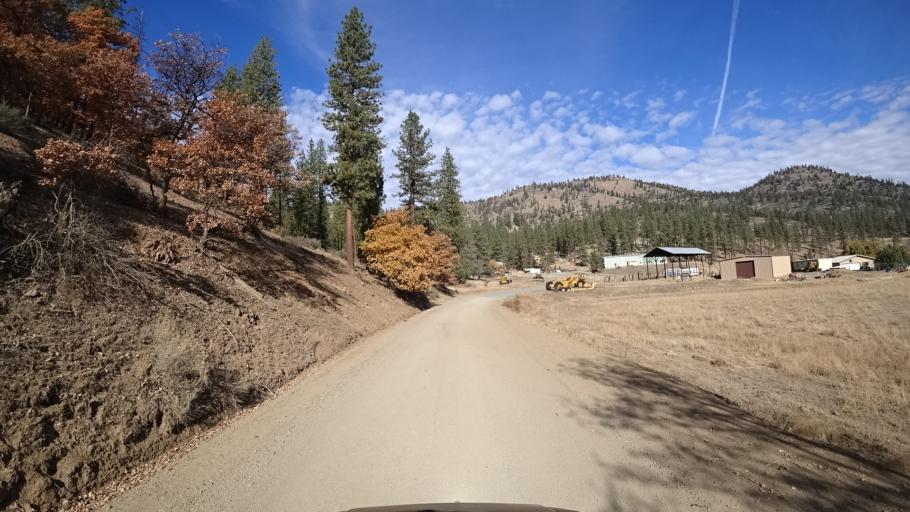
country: US
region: California
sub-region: Siskiyou County
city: Yreka
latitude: 41.6070
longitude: -122.7370
